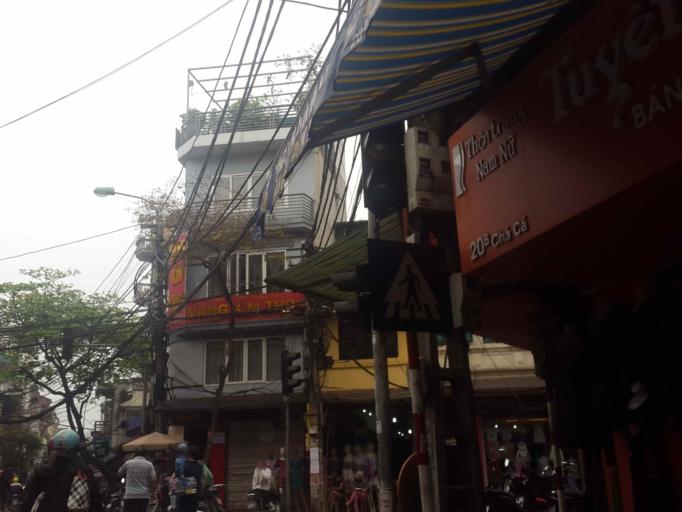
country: VN
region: Ha Noi
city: Hoan Kiem
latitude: 21.0354
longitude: 105.8492
